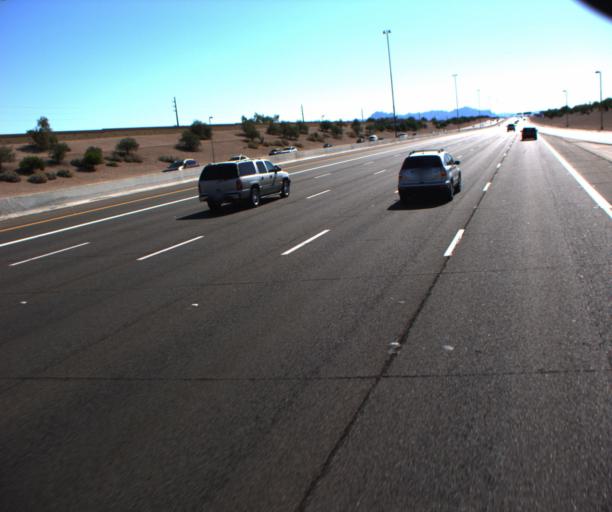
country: US
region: Arizona
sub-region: Maricopa County
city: Gilbert
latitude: 33.3864
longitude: -111.7164
